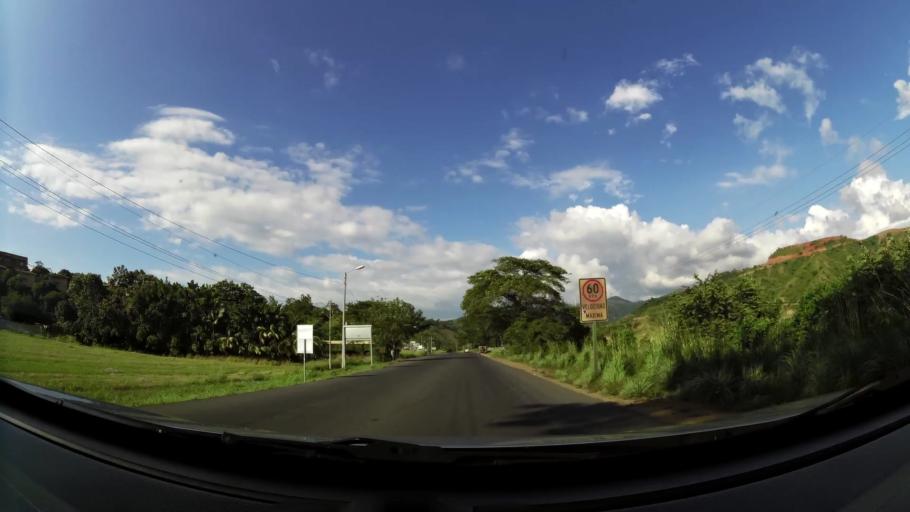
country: CR
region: Puntarenas
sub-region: Canton de Garabito
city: Jaco
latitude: 9.6364
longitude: -84.6273
